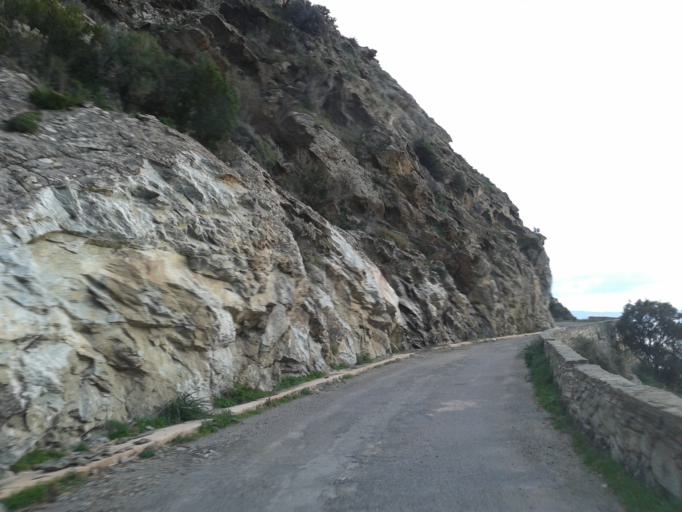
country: FR
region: Corsica
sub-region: Departement de la Haute-Corse
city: Brando
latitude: 42.8977
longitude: 9.3244
